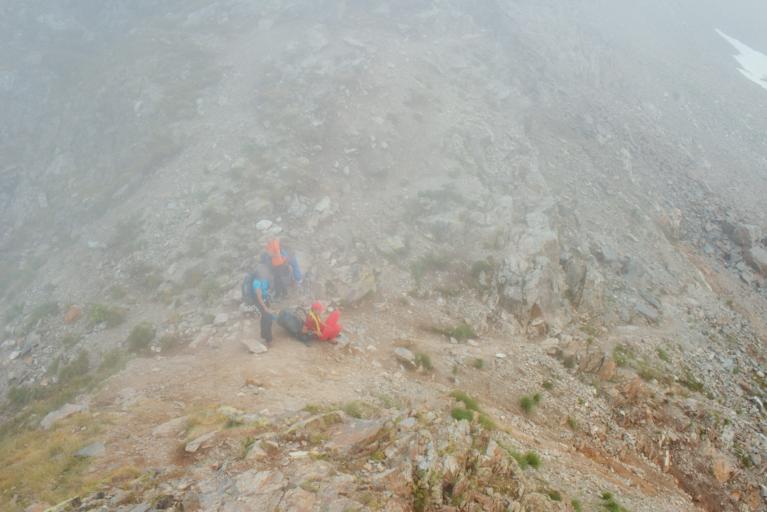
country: RU
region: Karachayevo-Cherkesiya
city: Nizhniy Arkhyz
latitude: 43.4484
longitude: 41.2326
